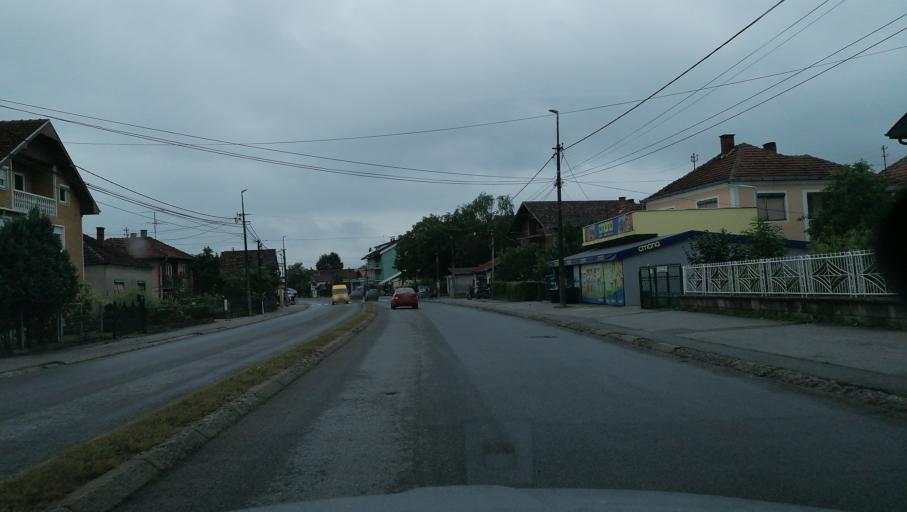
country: RS
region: Central Serbia
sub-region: Rasinski Okrug
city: Krusevac
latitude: 43.5843
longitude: 21.3048
